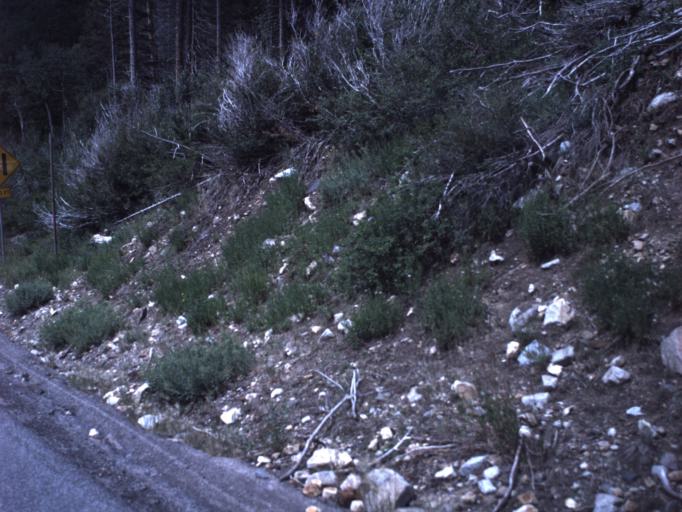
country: US
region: Utah
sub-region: Salt Lake County
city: Granite
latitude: 40.5783
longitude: -111.6721
